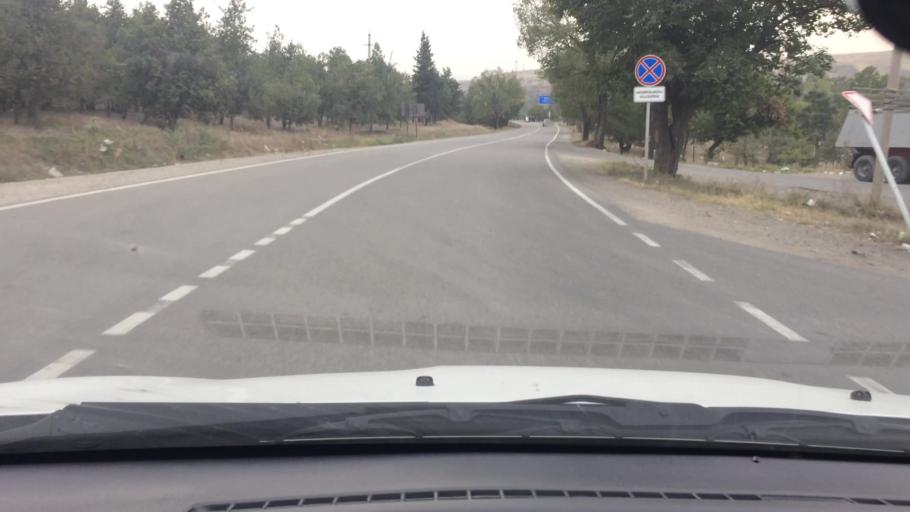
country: GE
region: Kvemo Kartli
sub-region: Gardabani
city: Gardabani
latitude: 41.3391
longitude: 45.0690
